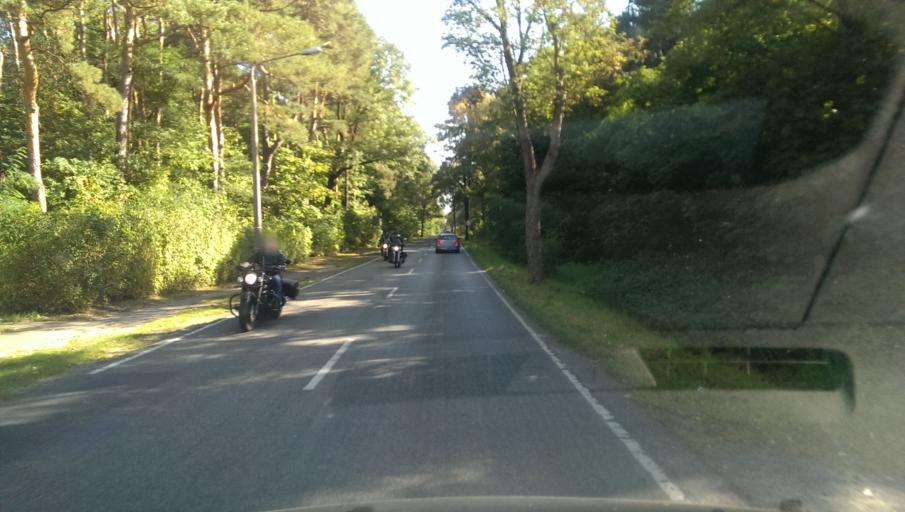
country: DE
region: Brandenburg
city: Teupitz
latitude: 52.1299
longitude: 13.6243
